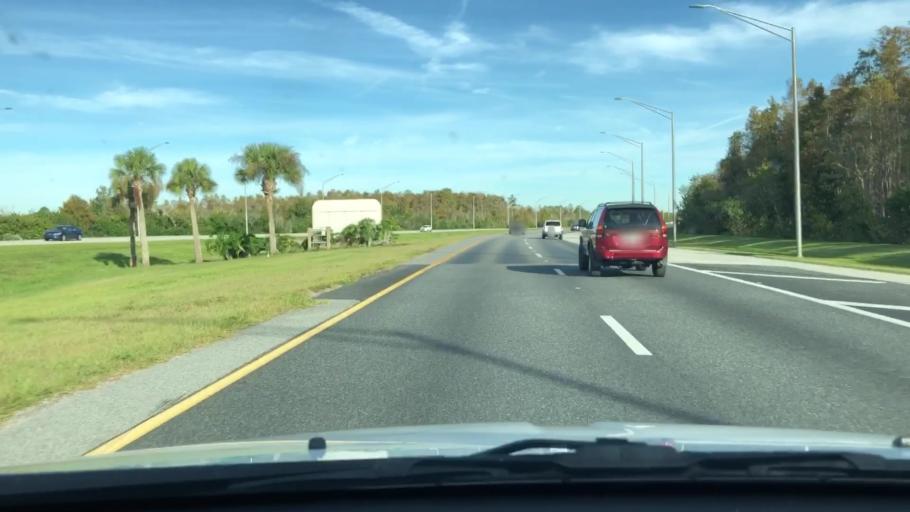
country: US
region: Florida
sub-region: Orange County
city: Meadow Woods
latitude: 28.3885
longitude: -81.3094
